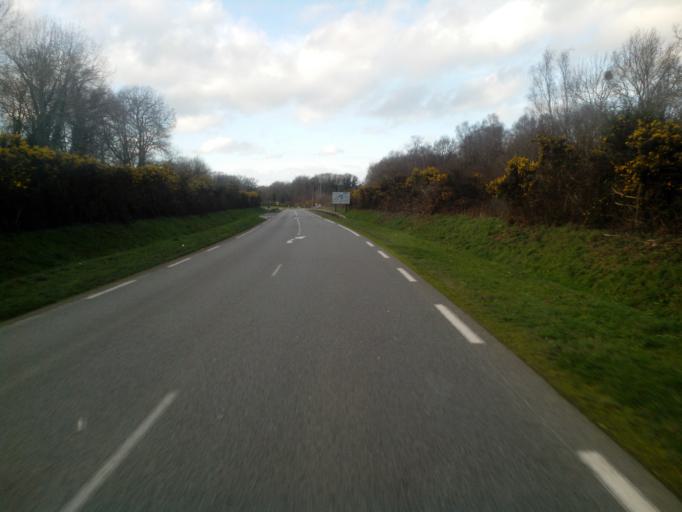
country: FR
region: Brittany
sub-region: Departement d'Ille-et-Vilaine
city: Pleurtuit
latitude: 48.5651
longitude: -2.0567
